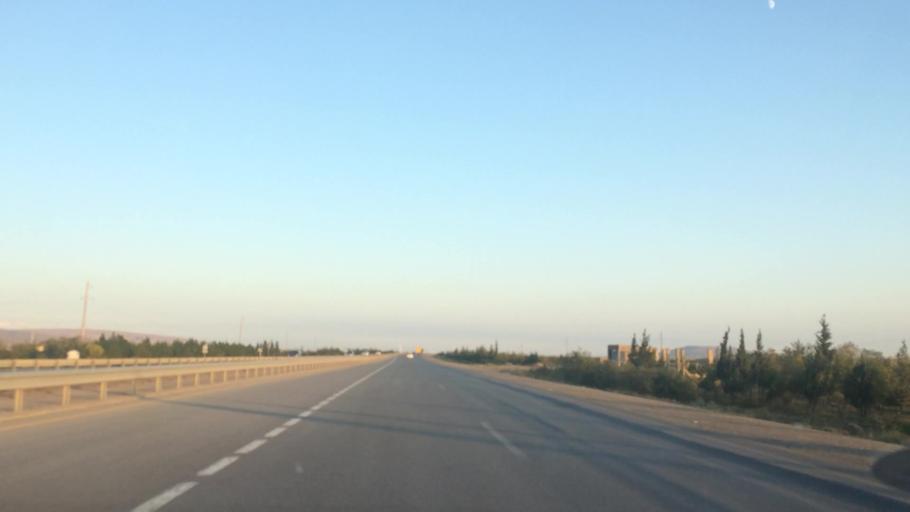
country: AZ
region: Haciqabul
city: Haciqabul
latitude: 40.0058
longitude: 49.1605
